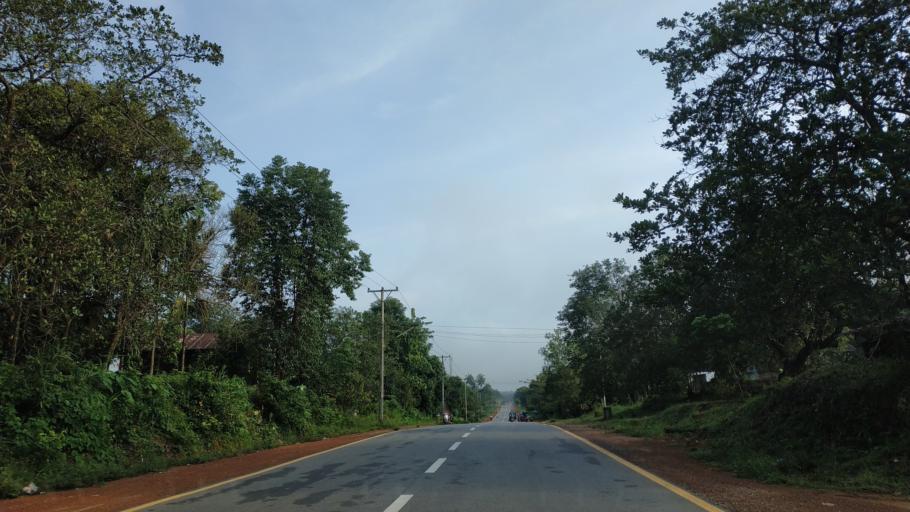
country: MM
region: Tanintharyi
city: Dawei
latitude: 14.2194
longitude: 98.2091
